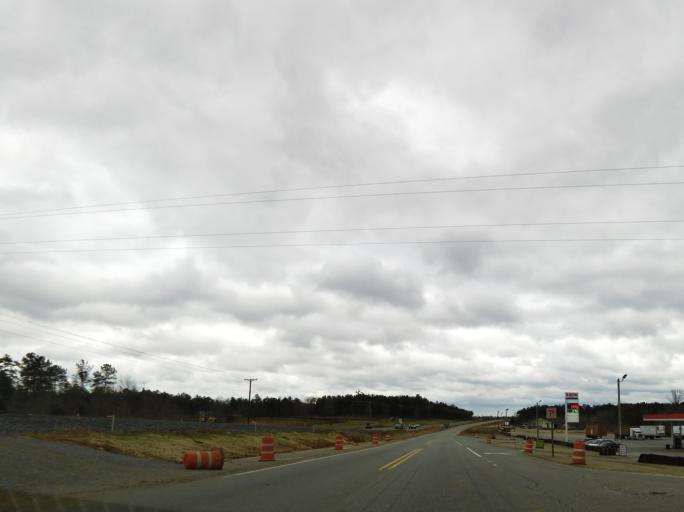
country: US
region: Georgia
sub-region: Twiggs County
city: Jeffersonville
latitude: 32.6212
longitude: -83.3699
